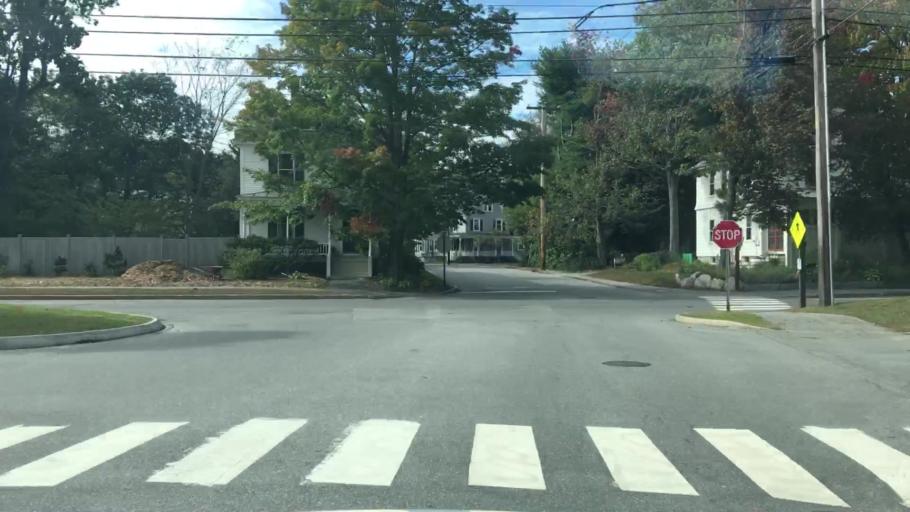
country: US
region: Maine
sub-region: Cumberland County
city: Brunswick
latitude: 43.9041
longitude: -69.9660
